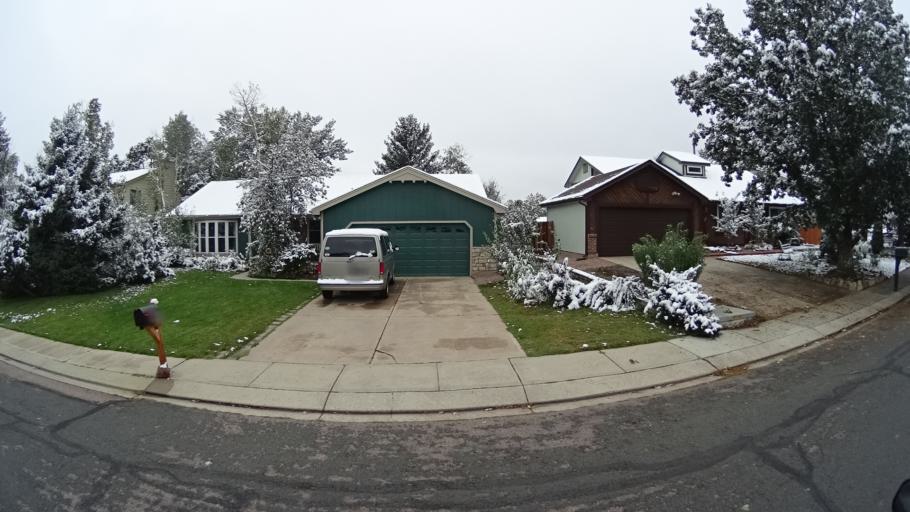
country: US
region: Colorado
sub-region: El Paso County
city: Colorado Springs
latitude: 38.9207
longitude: -104.7769
